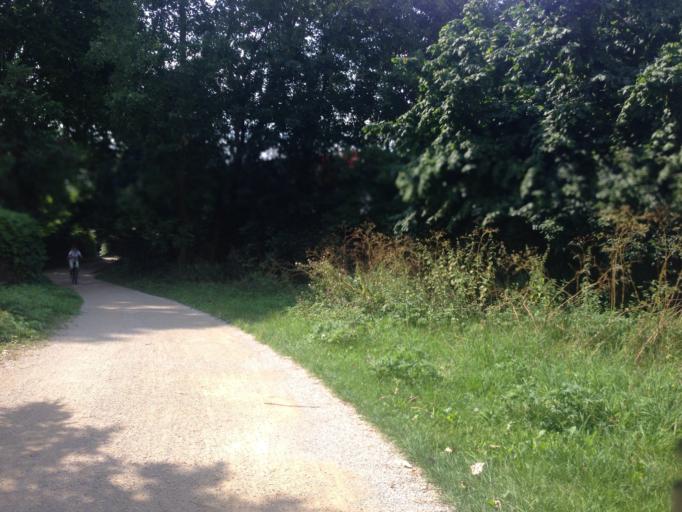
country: DE
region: Hesse
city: Niederrad
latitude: 50.1322
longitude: 8.6203
